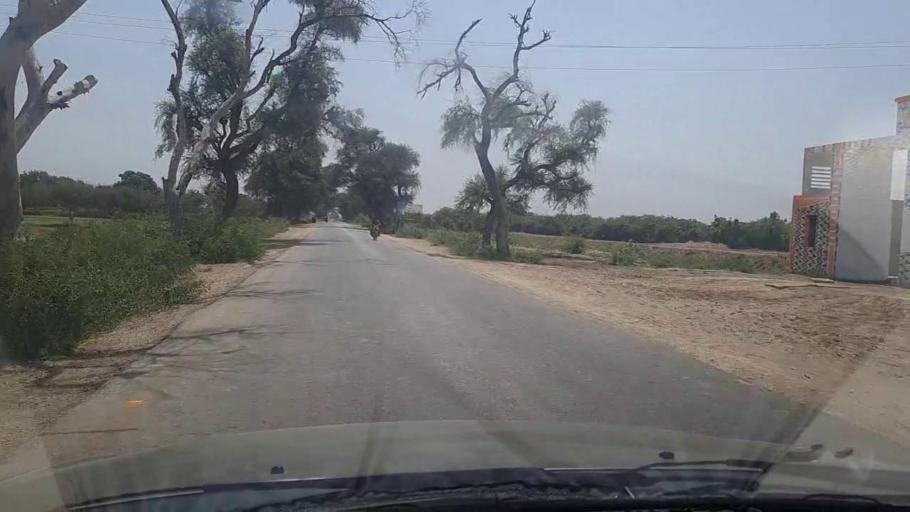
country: PK
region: Sindh
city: Tando Jam
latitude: 25.3716
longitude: 68.4713
